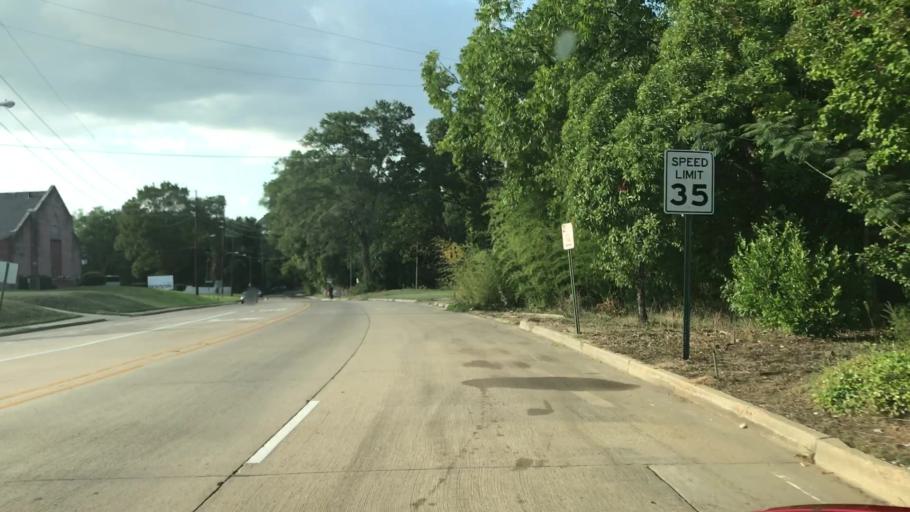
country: US
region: Louisiana
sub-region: Bossier Parish
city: Bossier City
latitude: 32.4554
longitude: -93.7544
